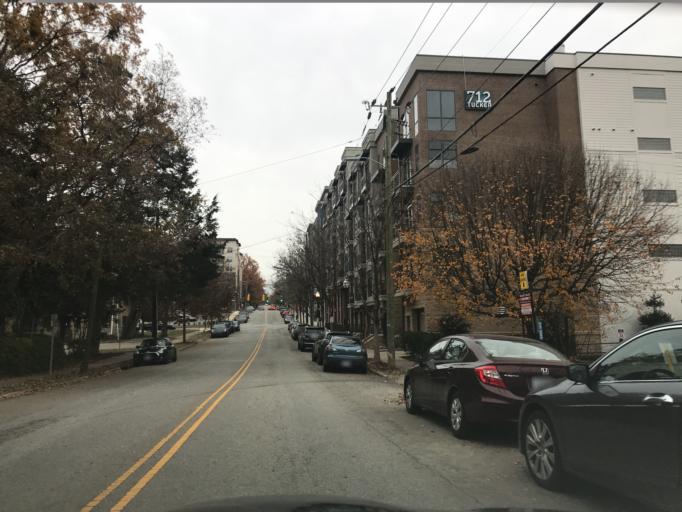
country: US
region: North Carolina
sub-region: Wake County
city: West Raleigh
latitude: 35.7873
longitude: -78.6489
